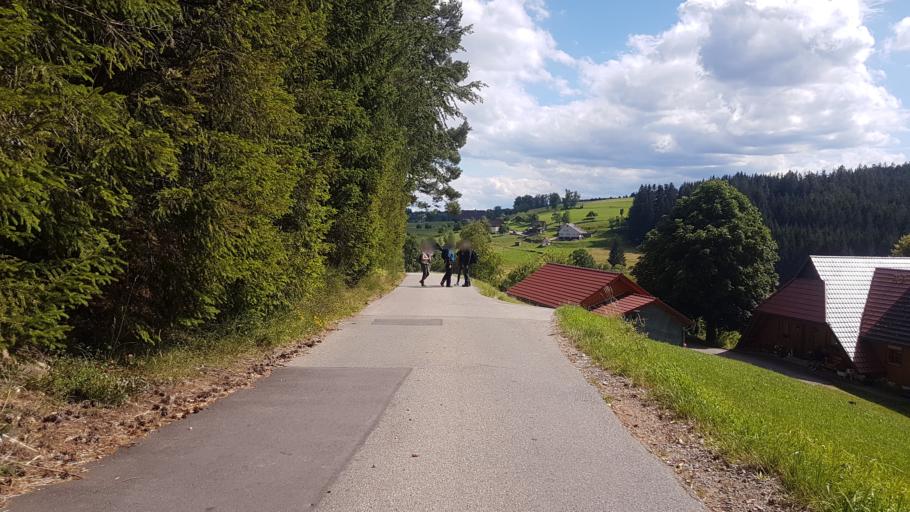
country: DE
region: Baden-Wuerttemberg
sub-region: Freiburg Region
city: Hardt
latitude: 48.1649
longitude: 8.4058
